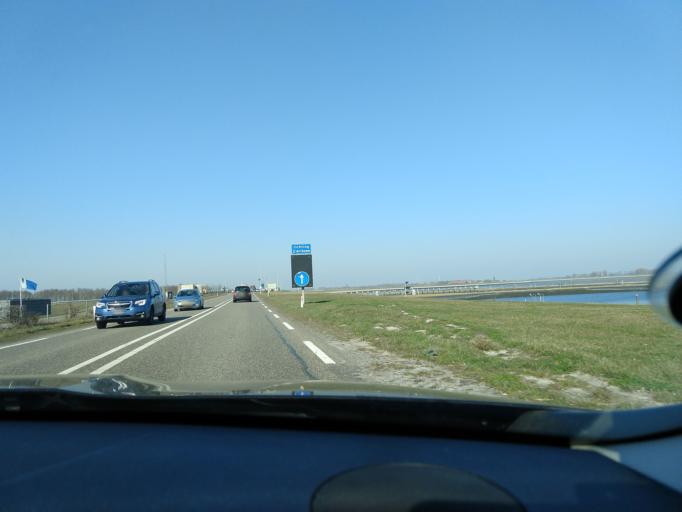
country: NL
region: Zeeland
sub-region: Gemeente Goes
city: Goes
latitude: 51.5412
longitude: 3.8662
